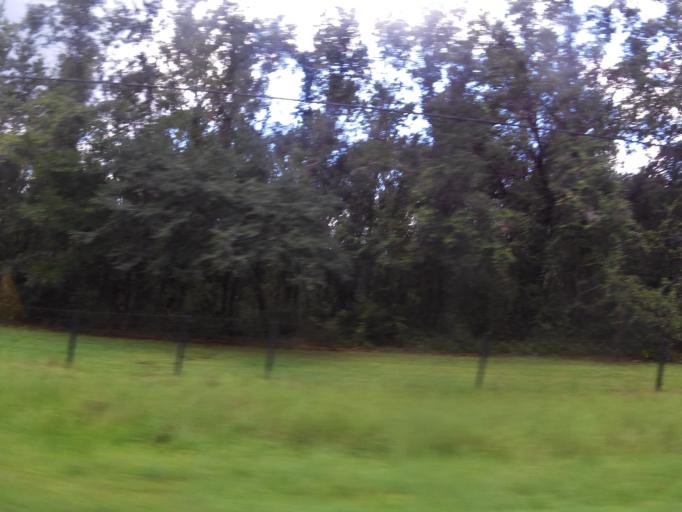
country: US
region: Florida
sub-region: Putnam County
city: East Palatka
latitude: 29.7866
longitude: -81.4840
